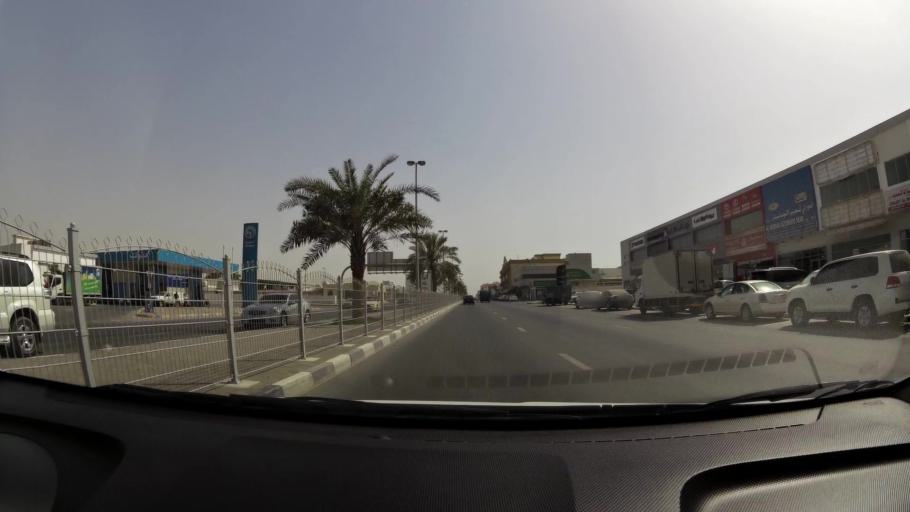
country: AE
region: Ash Shariqah
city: Sharjah
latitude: 25.3171
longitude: 55.4267
